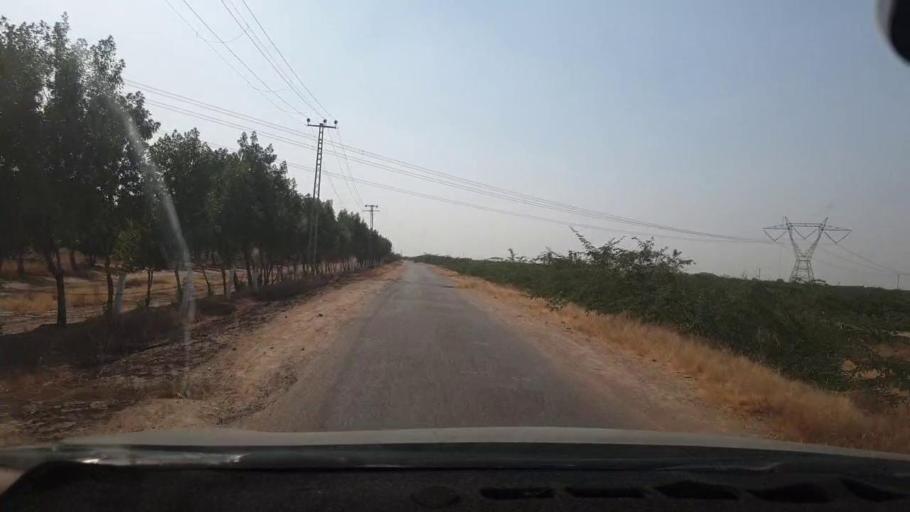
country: PK
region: Sindh
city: Malir Cantonment
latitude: 25.1115
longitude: 67.2056
